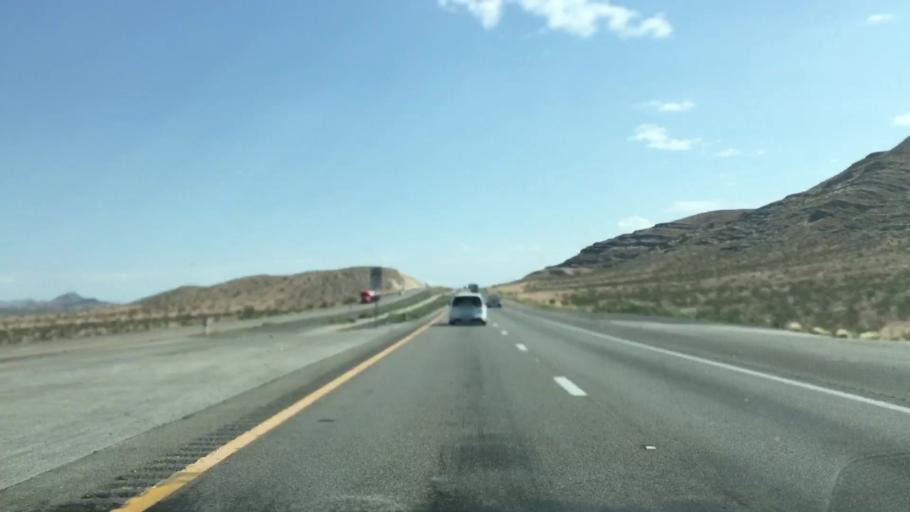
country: US
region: Nevada
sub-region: Clark County
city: Nellis Air Force Base
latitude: 36.4563
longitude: -114.8389
